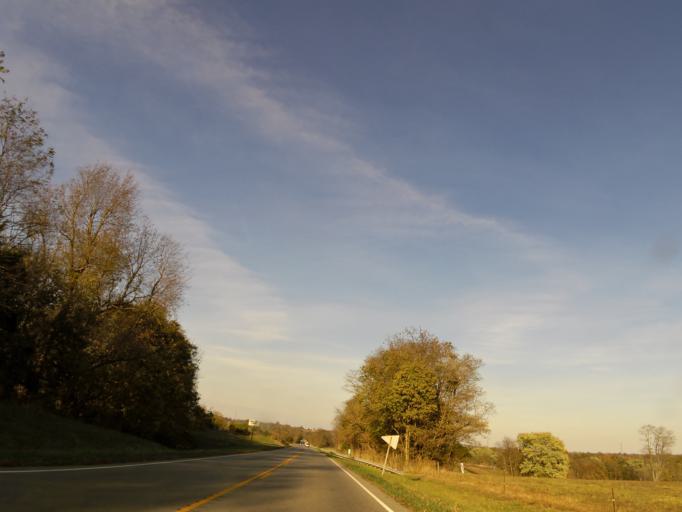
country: US
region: Kentucky
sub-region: Lincoln County
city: Stanford
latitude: 37.5595
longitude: -84.6273
